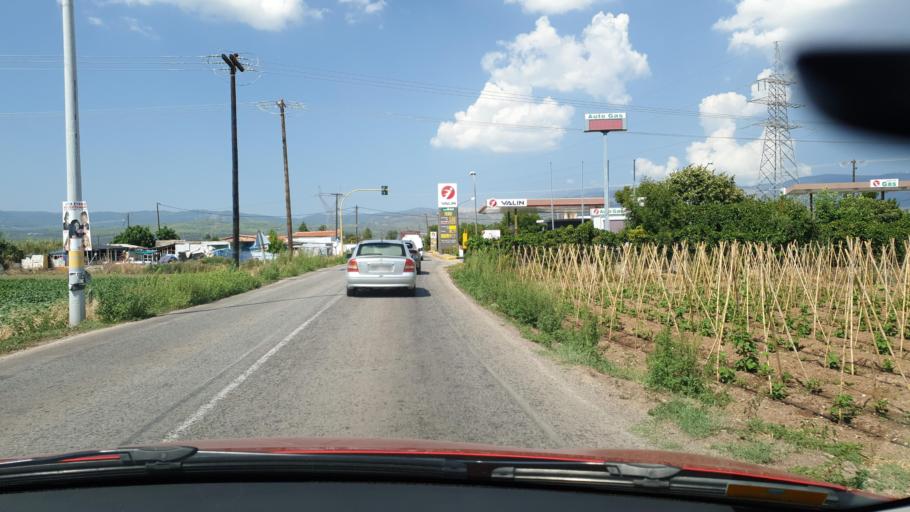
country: GR
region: Central Greece
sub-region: Nomos Evvoias
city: Kastella
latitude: 38.5582
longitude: 23.6327
